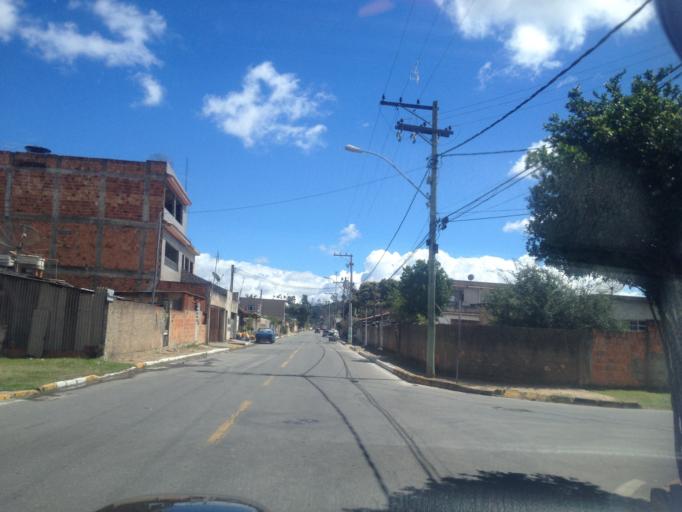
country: BR
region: Rio de Janeiro
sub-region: Porto Real
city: Porto Real
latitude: -22.4458
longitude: -44.3109
